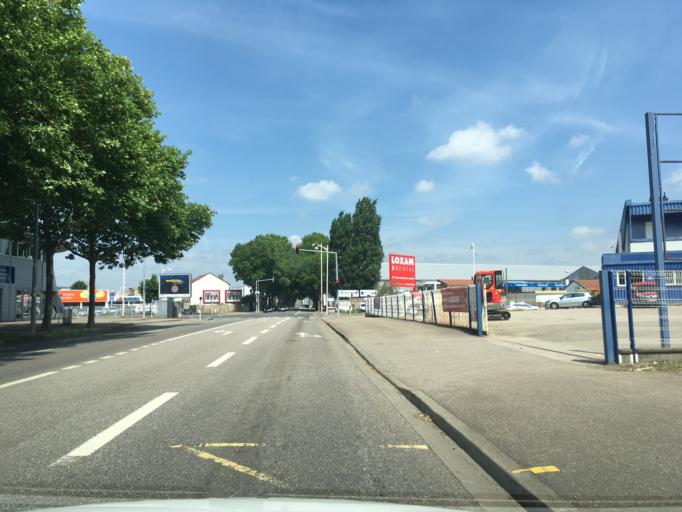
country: FR
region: Lorraine
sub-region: Departement de Meurthe-et-Moselle
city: Tomblaine
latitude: 48.6828
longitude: 6.2031
